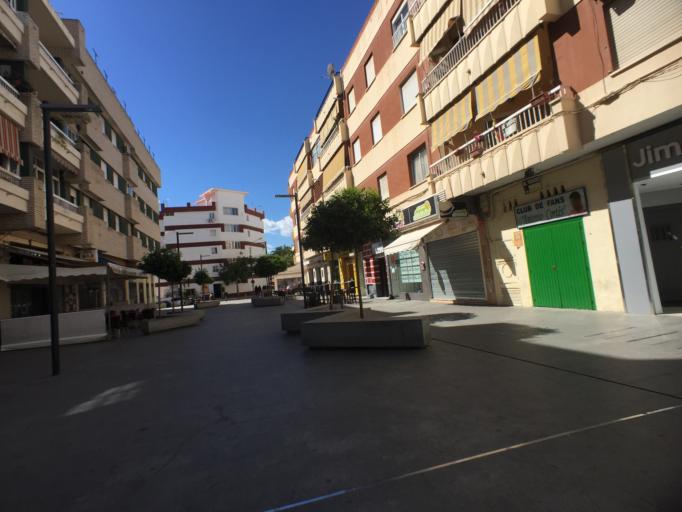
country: ES
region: Andalusia
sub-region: Provincia de Malaga
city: Nerja
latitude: 36.7449
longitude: -3.8806
